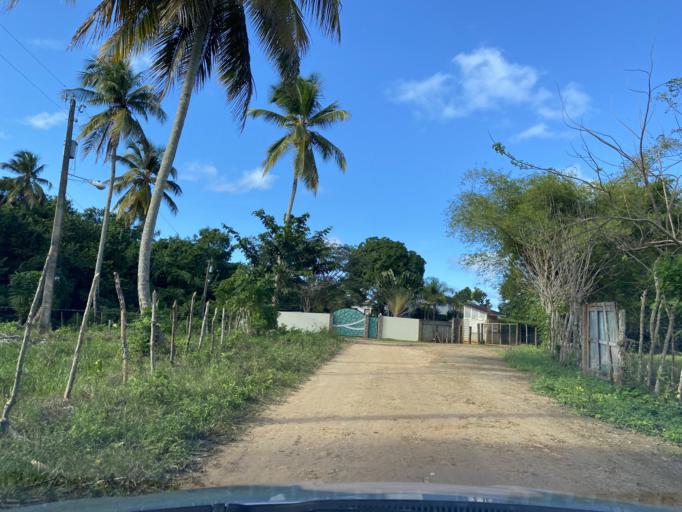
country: DO
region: Samana
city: Las Terrenas
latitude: 19.3090
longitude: -69.5587
